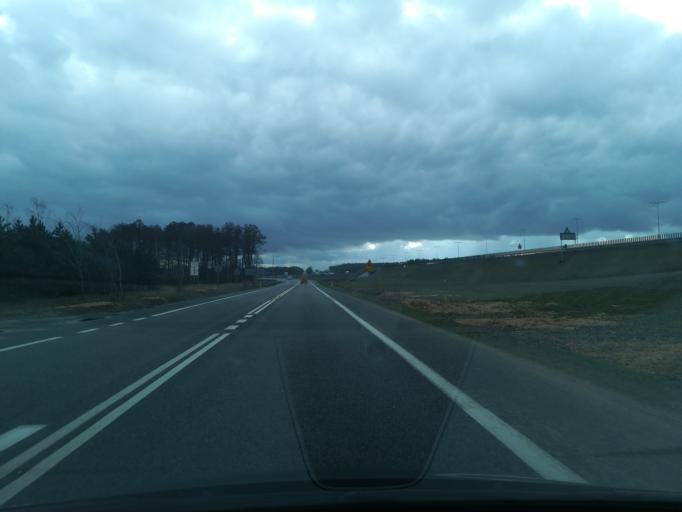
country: PL
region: Kujawsko-Pomorskie
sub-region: Powiat aleksandrowski
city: Ciechocinek
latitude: 52.8697
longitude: 18.7573
